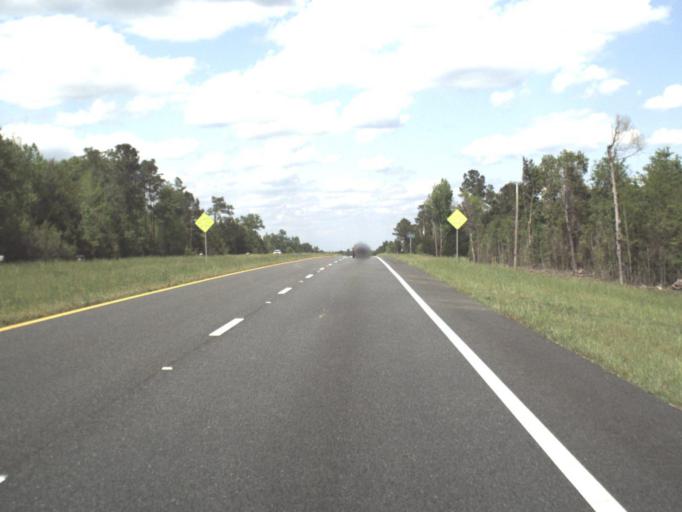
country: US
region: Florida
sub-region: Escambia County
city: Molino
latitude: 30.8351
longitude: -87.3288
